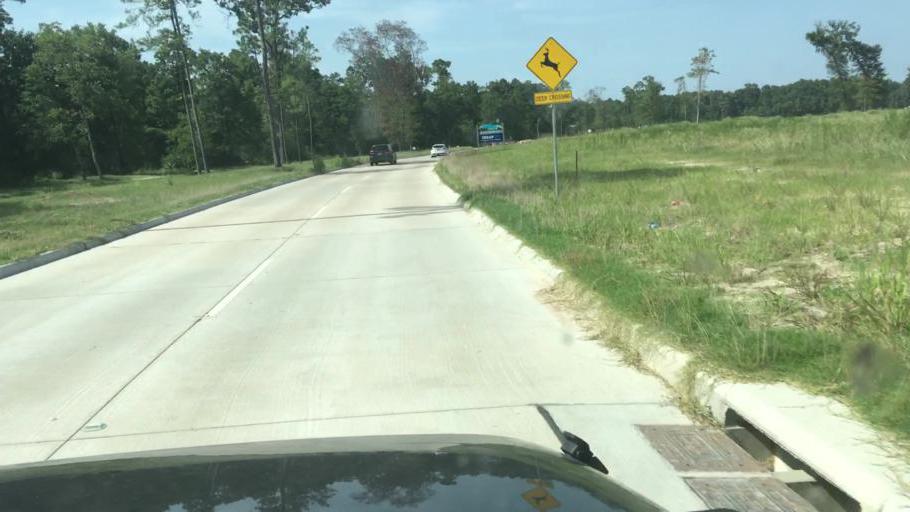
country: US
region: Texas
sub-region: Harris County
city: Atascocita
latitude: 29.9490
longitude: -95.2109
